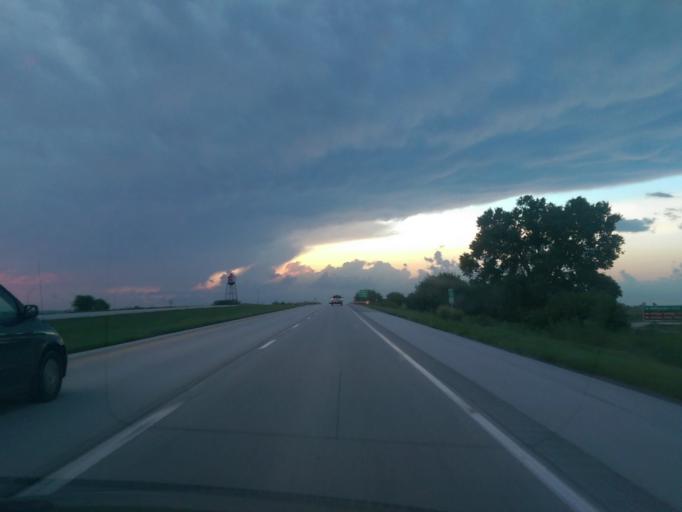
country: US
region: Nebraska
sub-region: Otoe County
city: Nebraska City
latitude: 40.6873
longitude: -95.7814
